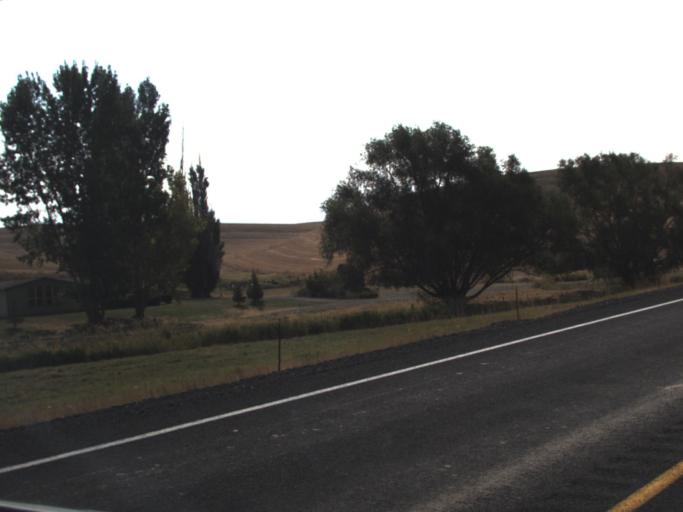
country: US
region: Washington
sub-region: Whitman County
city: Pullman
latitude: 46.7859
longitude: -117.1484
